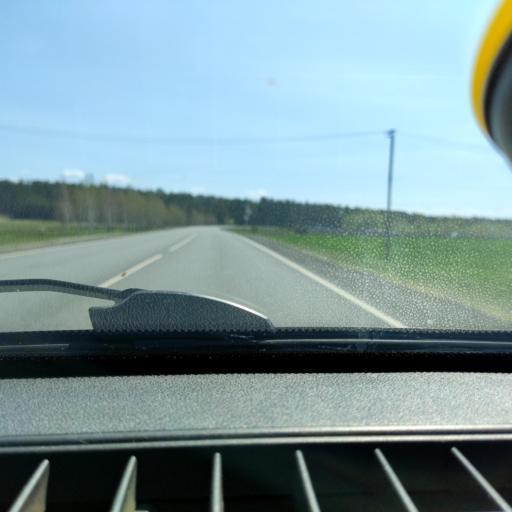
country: RU
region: Samara
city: Povolzhskiy
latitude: 53.6340
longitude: 49.6585
